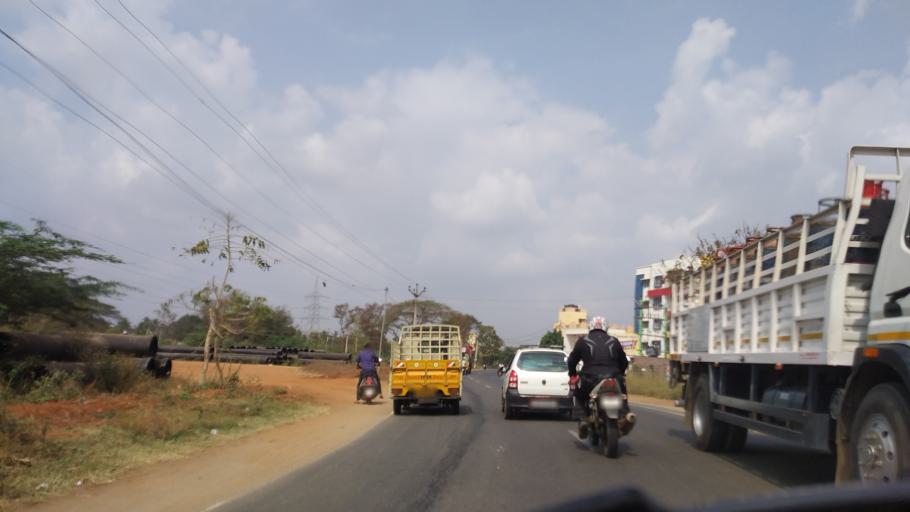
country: IN
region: Tamil Nadu
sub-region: Coimbatore
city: Perur
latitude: 10.9445
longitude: 76.9393
